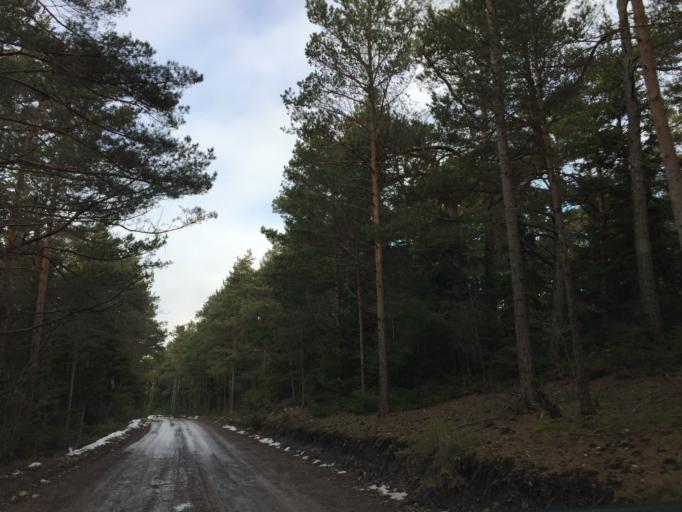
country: EE
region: Saare
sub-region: Kuressaare linn
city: Kuressaare
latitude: 58.4904
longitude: 21.9352
